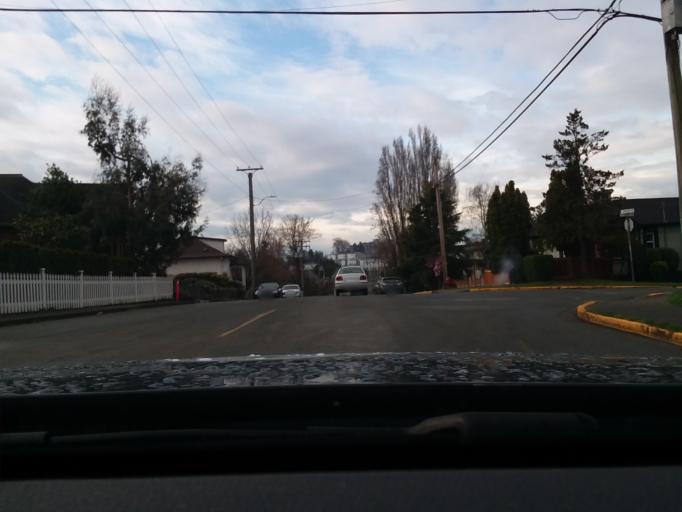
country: CA
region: British Columbia
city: Victoria
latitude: 48.4376
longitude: -123.3936
